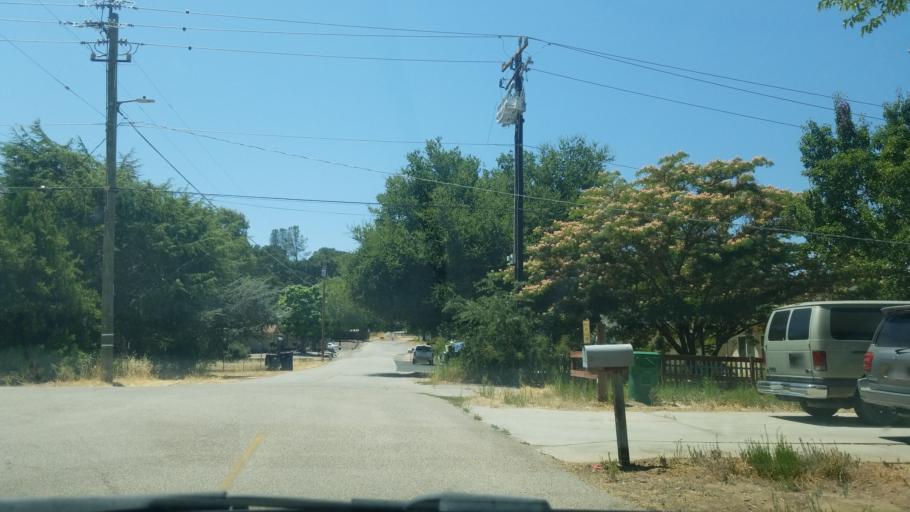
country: US
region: California
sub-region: San Luis Obispo County
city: Atascadero
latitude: 35.5087
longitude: -120.6659
